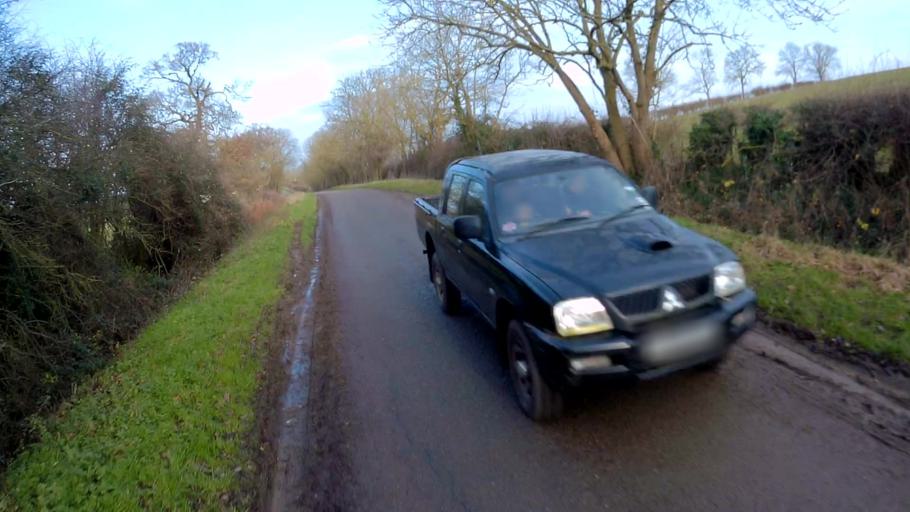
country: GB
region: England
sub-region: Lincolnshire
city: Bourne
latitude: 52.7471
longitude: -0.4177
